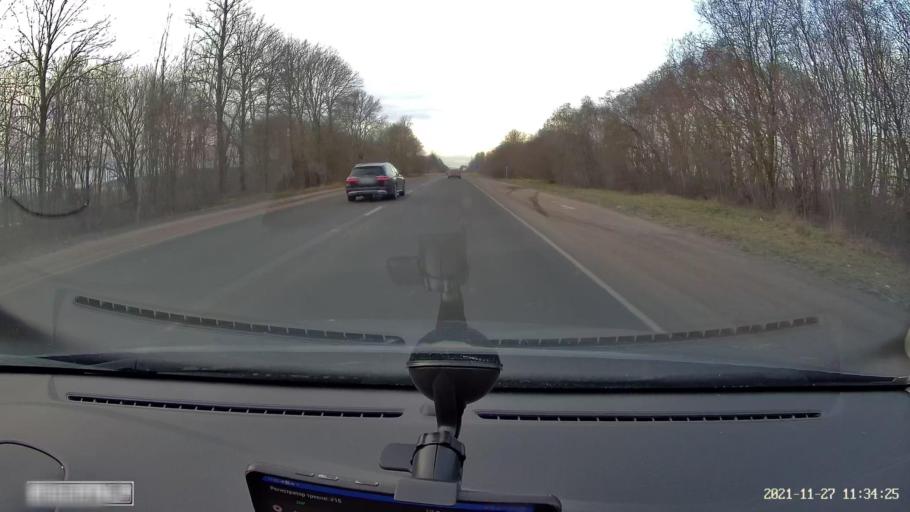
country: RU
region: Leningrad
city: Russko-Vysotskoye
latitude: 59.7067
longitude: 30.0012
